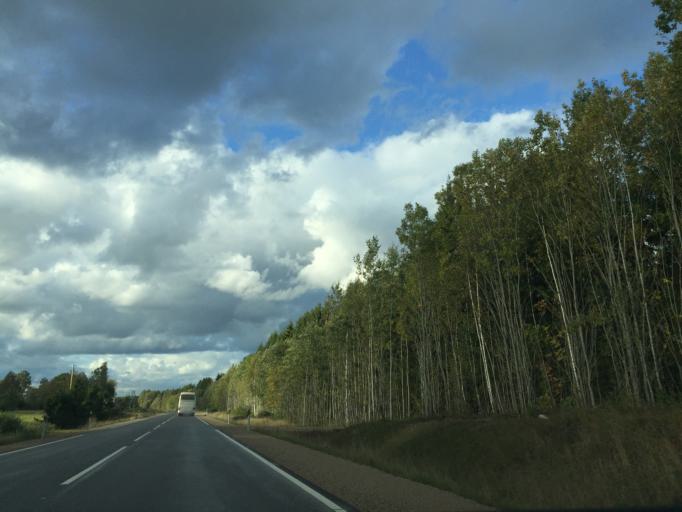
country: LV
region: Ligatne
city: Ligatne
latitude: 57.1407
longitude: 25.0807
